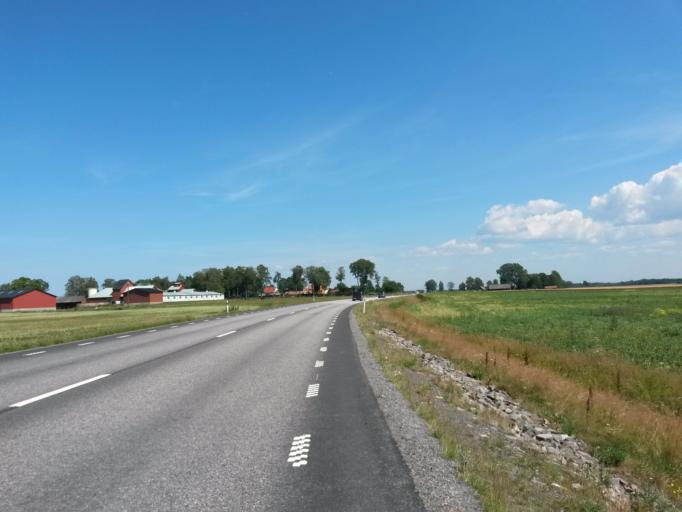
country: SE
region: Vaestra Goetaland
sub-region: Lidkopings Kommun
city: Lidkoping
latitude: 58.4794
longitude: 13.0840
